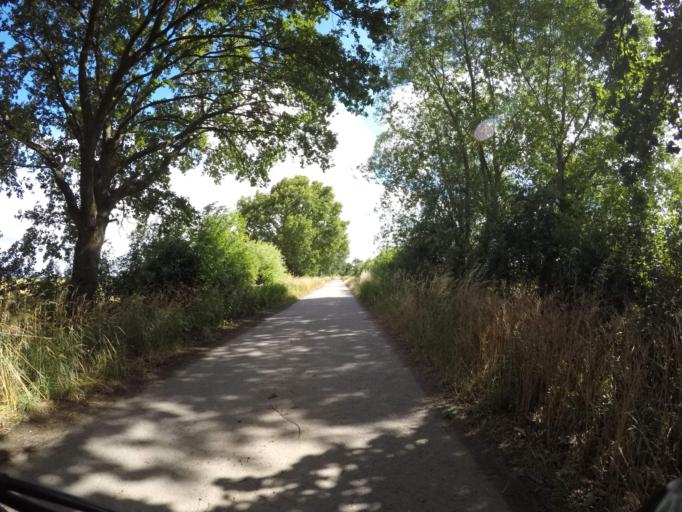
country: DE
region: Lower Saxony
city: Hitzacker
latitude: 53.1665
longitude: 11.0587
